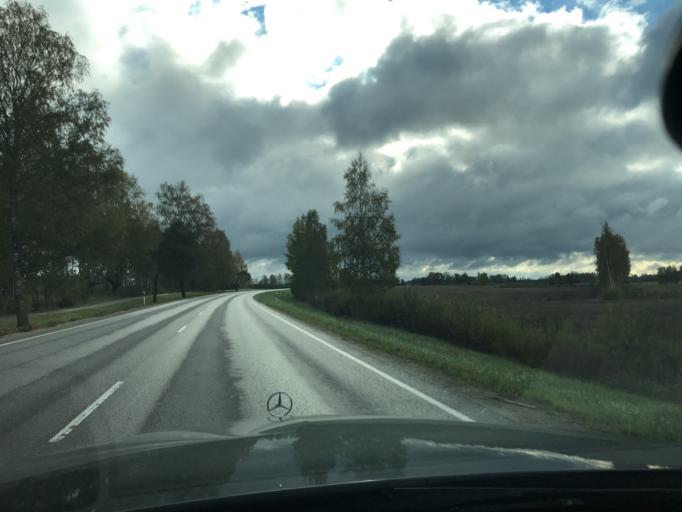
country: EE
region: Valgamaa
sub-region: Torva linn
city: Torva
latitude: 58.0287
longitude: 25.8584
